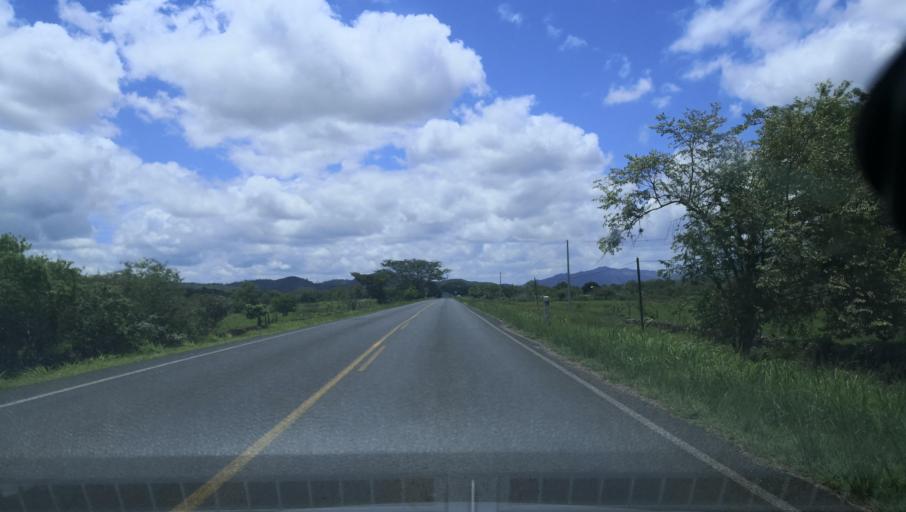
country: NI
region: Esteli
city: Esteli
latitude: 13.2214
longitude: -86.3795
